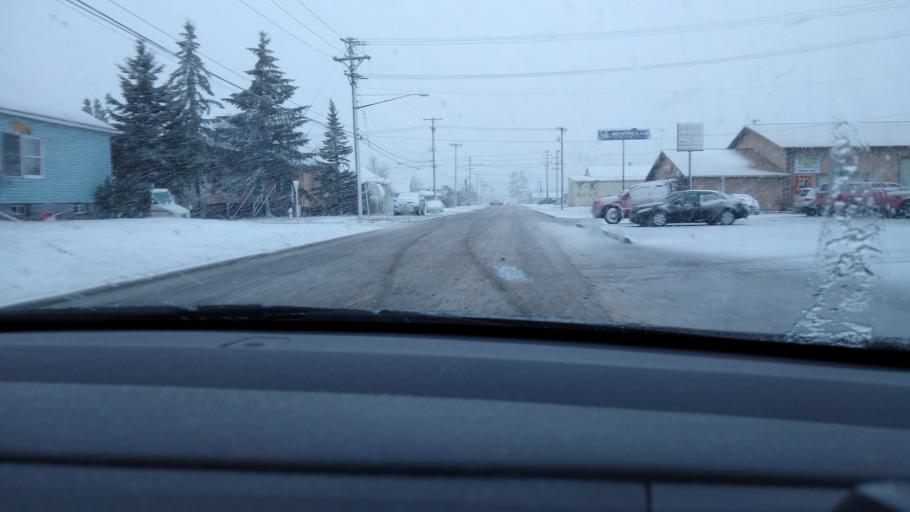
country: US
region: Michigan
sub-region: Delta County
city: Escanaba
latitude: 45.7536
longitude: -87.0740
